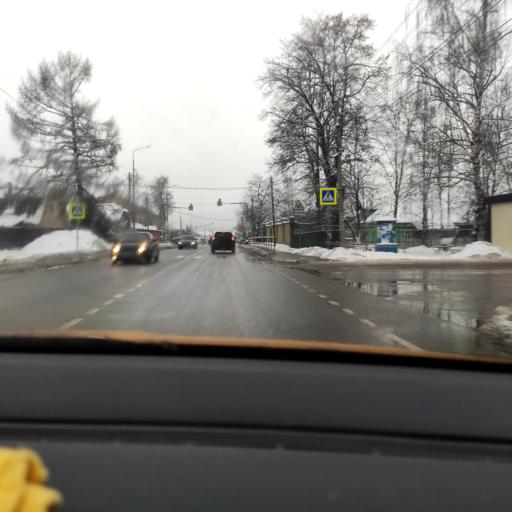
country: RU
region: Moskovskaya
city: Rozhdestveno
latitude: 55.8106
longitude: 37.0093
